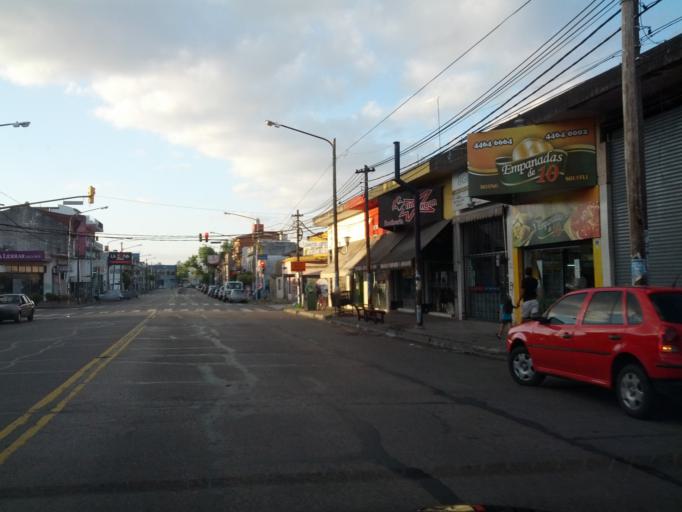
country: AR
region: Buenos Aires
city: San Justo
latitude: -34.6545
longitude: -58.5499
